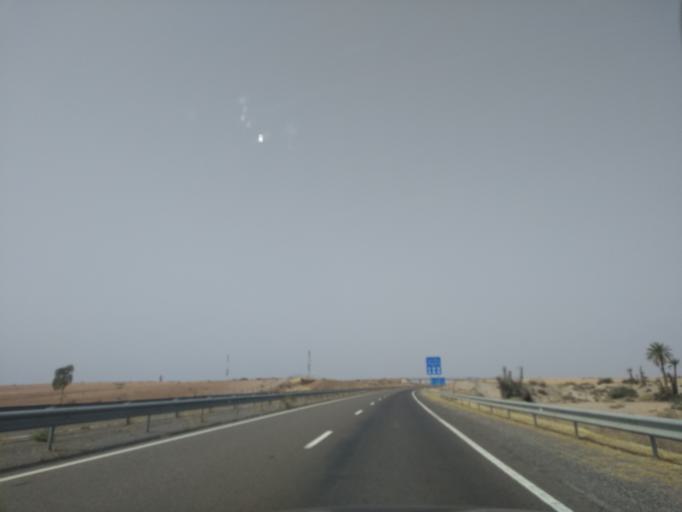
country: MA
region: Marrakech-Tensift-Al Haouz
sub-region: Marrakech
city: Marrakesh
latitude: 31.7260
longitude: -8.2230
